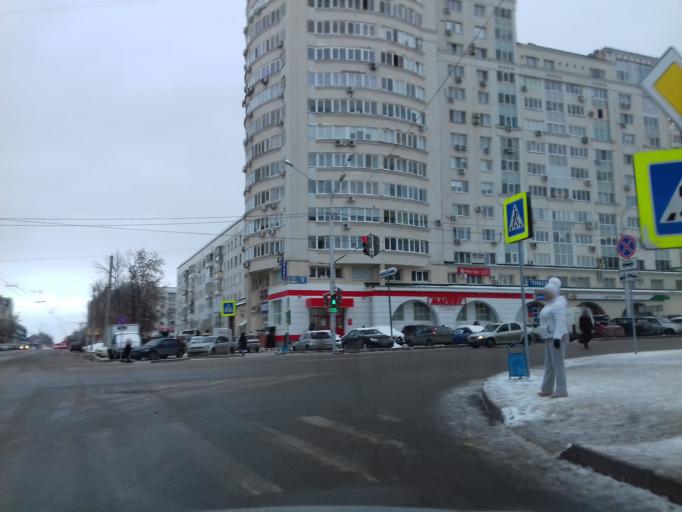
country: RU
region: Bashkortostan
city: Ufa
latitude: 54.7245
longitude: 55.9277
